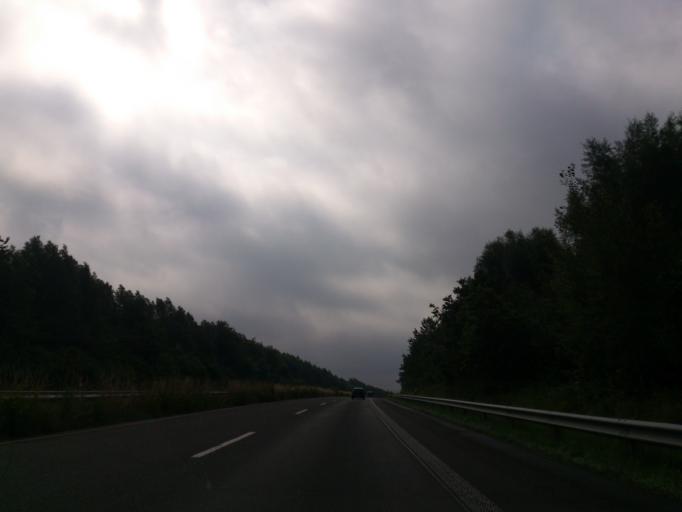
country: DE
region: Schleswig-Holstein
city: Arkebek
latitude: 54.1561
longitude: 9.2291
